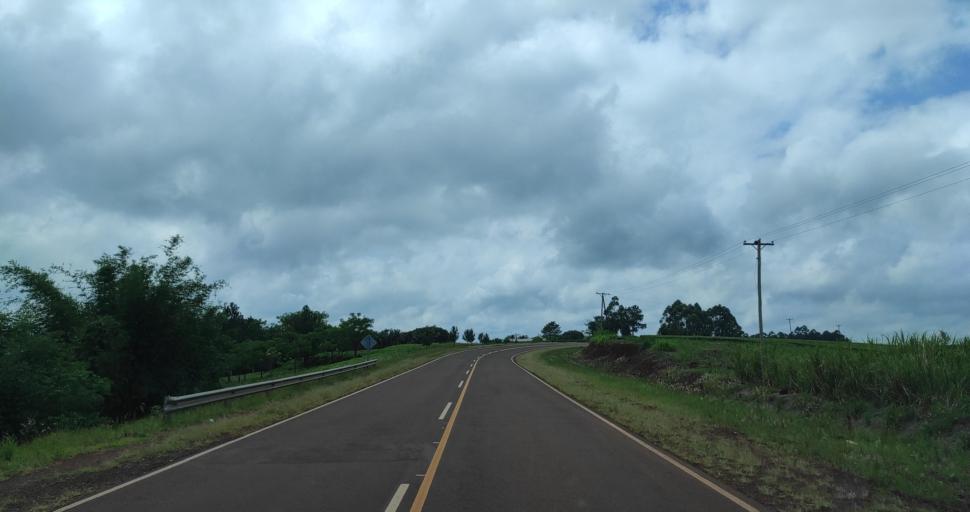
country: AR
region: Misiones
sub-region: Departamento de Veinticinco de Mayo
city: Veinticinco de Mayo
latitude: -27.3459
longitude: -54.8763
